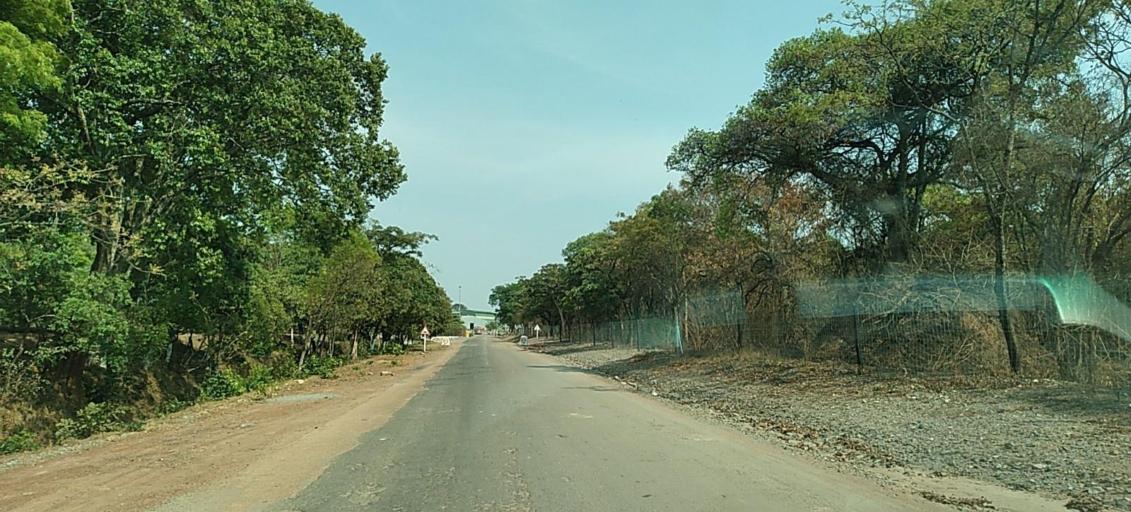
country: ZM
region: Copperbelt
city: Chililabombwe
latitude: -12.3001
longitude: 27.7751
